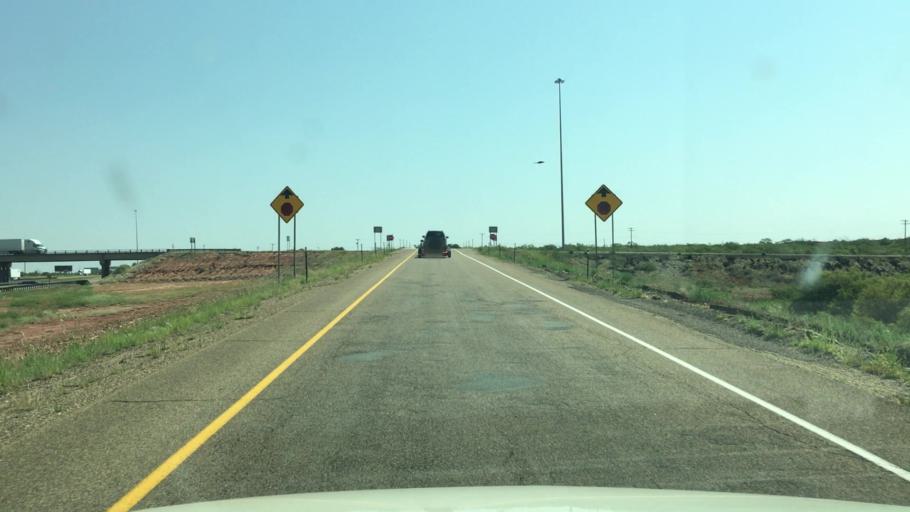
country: US
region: New Mexico
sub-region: Quay County
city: Tucumcari
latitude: 35.1546
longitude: -103.7046
